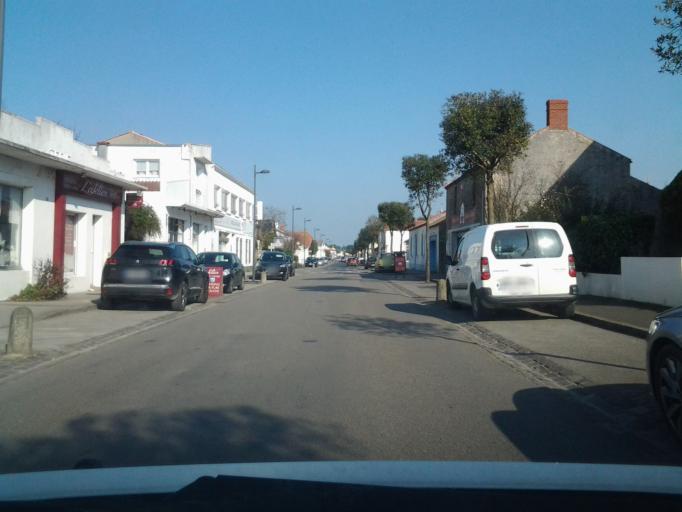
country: FR
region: Pays de la Loire
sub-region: Departement de la Vendee
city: La Gueriniere
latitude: 47.0036
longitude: -2.2439
